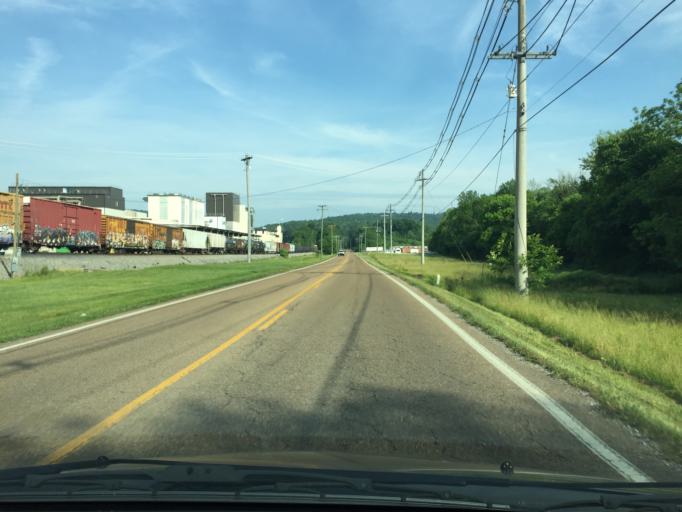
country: US
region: Tennessee
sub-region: Hamilton County
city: Collegedale
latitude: 35.0487
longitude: -85.0381
